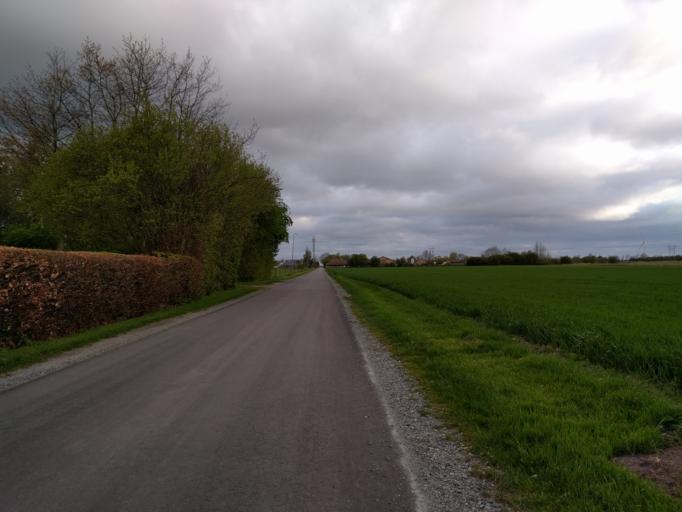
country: DK
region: South Denmark
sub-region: Odense Kommune
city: Bullerup
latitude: 55.4435
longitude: 10.4996
